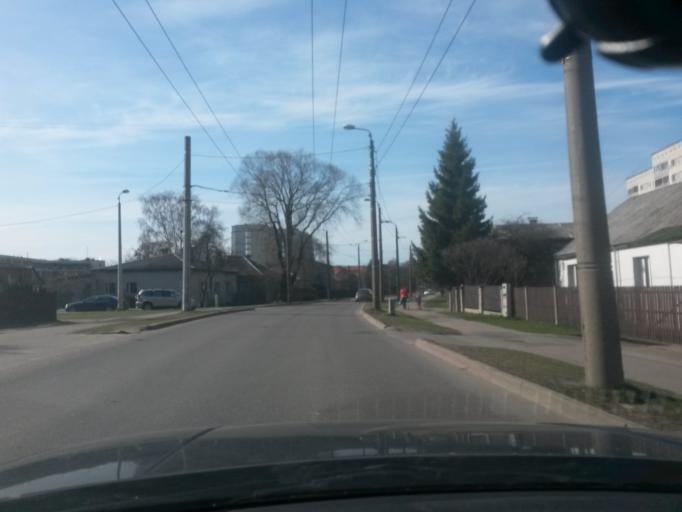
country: LV
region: Kekava
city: Kekava
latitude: 56.9069
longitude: 24.1998
